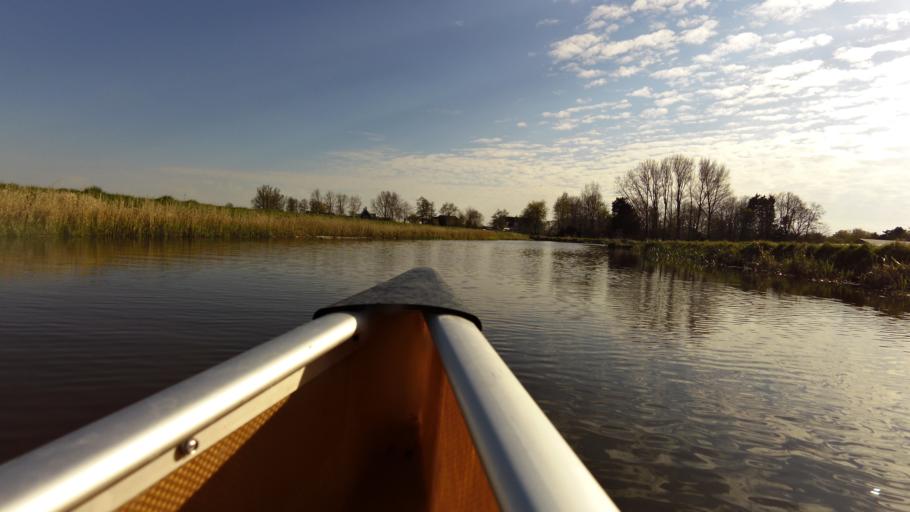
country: NL
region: South Holland
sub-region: Gemeente Teylingen
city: Sassenheim
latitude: 52.2329
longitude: 4.5392
